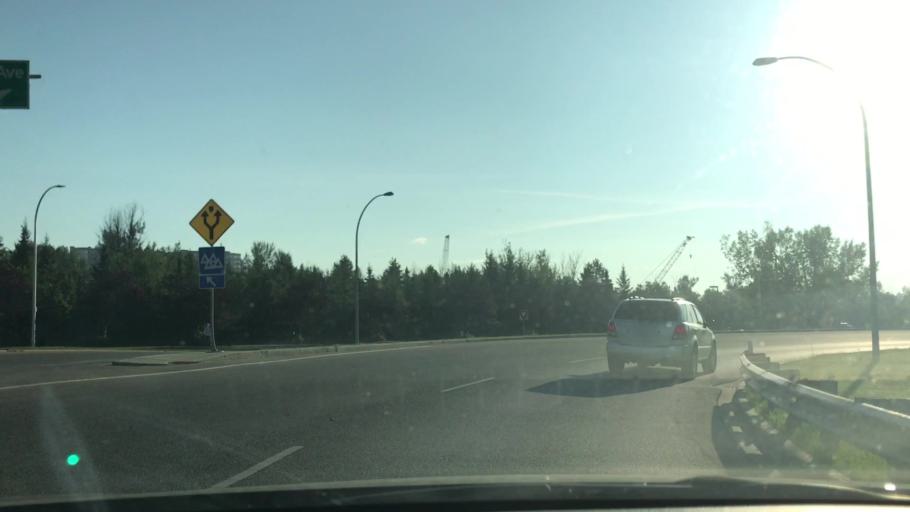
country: CA
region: Alberta
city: Edmonton
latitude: 53.5377
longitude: -113.4837
